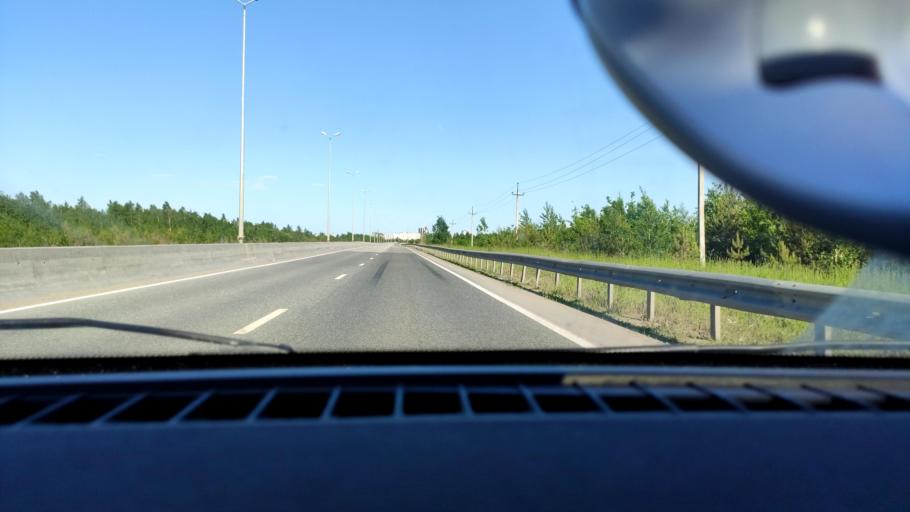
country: RU
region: Perm
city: Kondratovo
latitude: 58.0041
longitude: 56.0717
